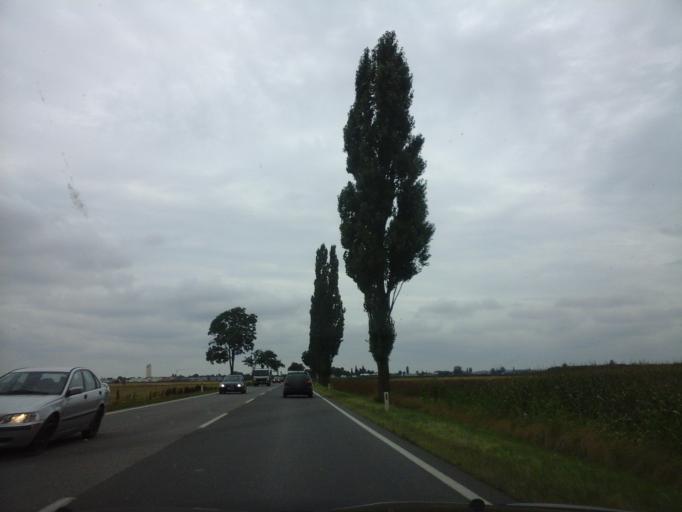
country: AT
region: Lower Austria
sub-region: Politischer Bezirk Ganserndorf
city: Engelhartstetten
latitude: 48.1646
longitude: 16.8956
